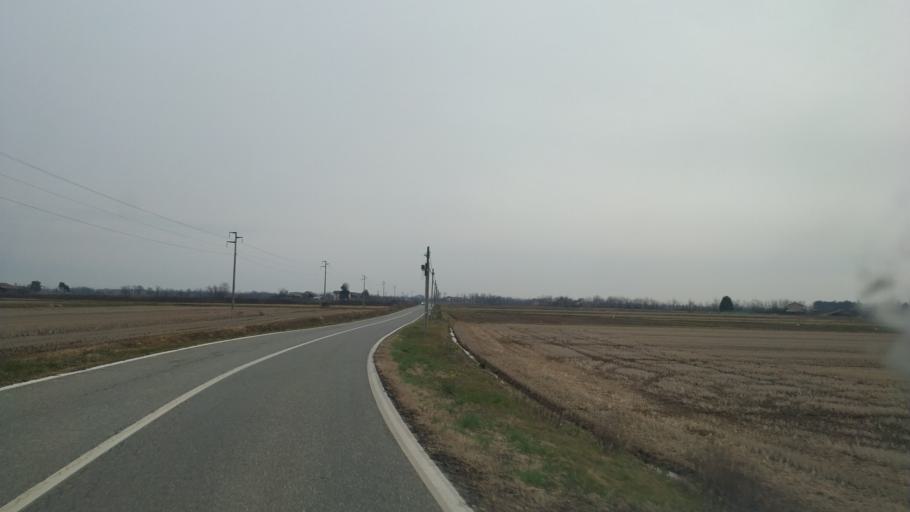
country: IT
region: Piedmont
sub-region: Provincia di Vercelli
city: Buronzo
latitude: 45.4904
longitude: 8.2871
